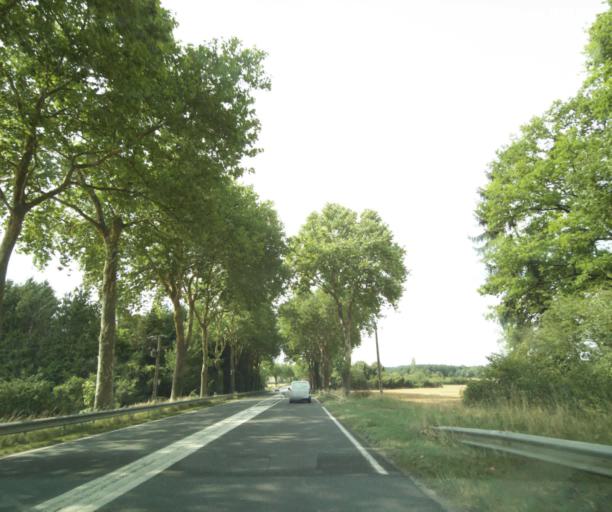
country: FR
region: Centre
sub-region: Departement d'Indre-et-Loire
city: Charentilly
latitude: 47.4721
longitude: 0.6164
